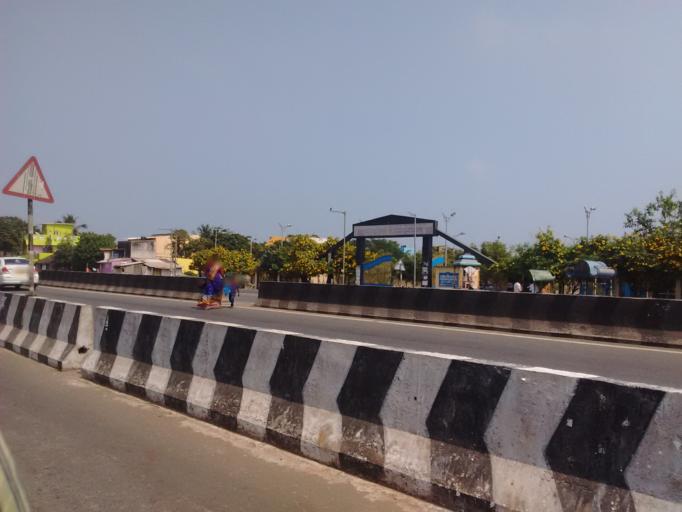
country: IN
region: Tamil Nadu
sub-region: Thiruvallur
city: Tiruvottiyur
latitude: 13.1615
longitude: 80.3061
